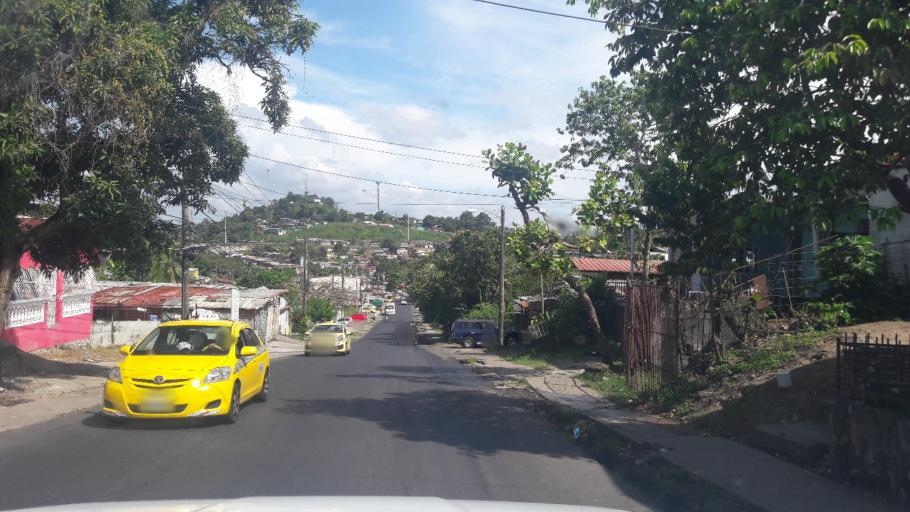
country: PA
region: Panama
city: San Miguelito
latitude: 9.0656
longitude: -79.4883
